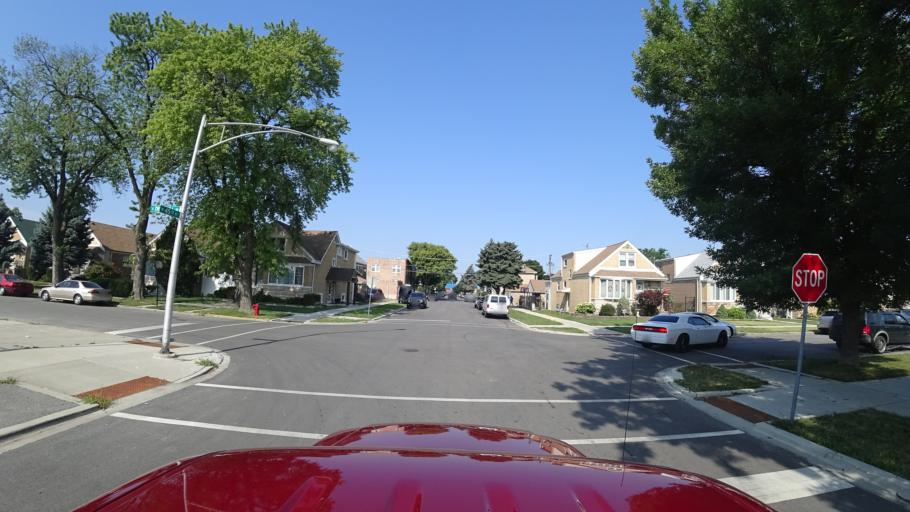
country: US
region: Illinois
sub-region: Cook County
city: Cicero
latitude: 41.8117
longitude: -87.7100
